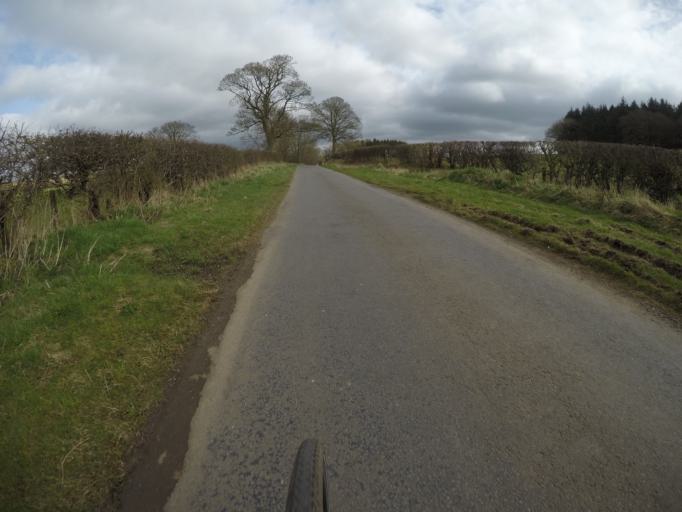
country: GB
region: Scotland
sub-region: North Ayrshire
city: Irvine
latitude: 55.6427
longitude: -4.6273
